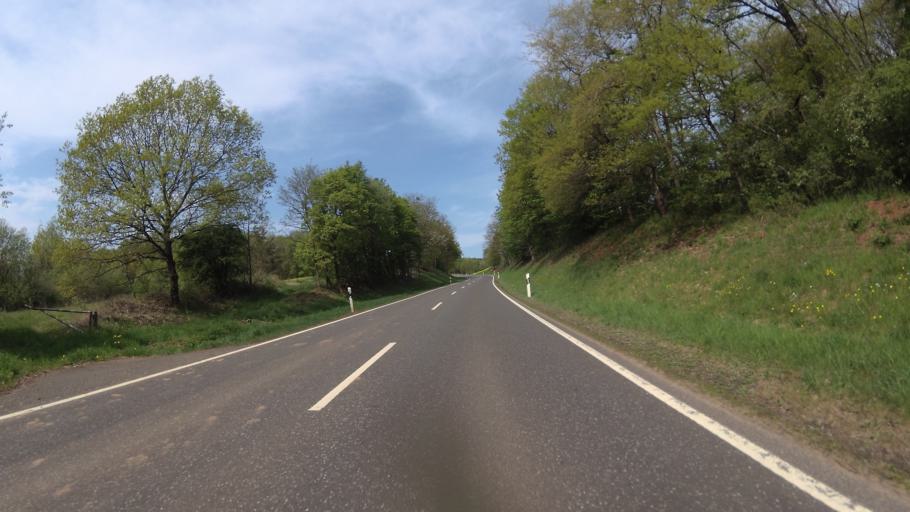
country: DE
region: Rheinland-Pfalz
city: Bausendorf
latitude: 50.0188
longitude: 7.0069
